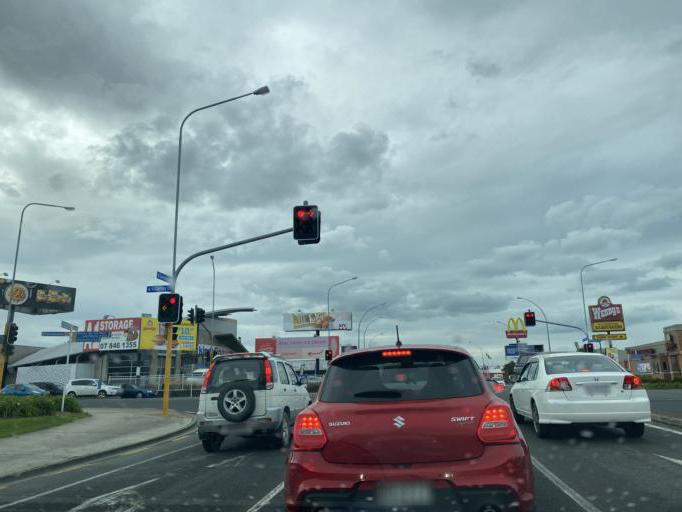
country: NZ
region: Waikato
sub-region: Hamilton City
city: Hamilton
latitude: -37.7952
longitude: 175.2606
